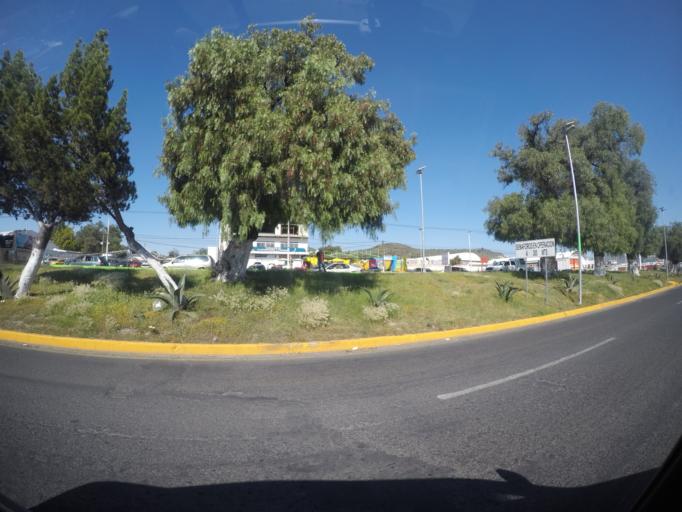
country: MX
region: Hidalgo
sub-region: Mineral de la Reforma
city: Carboneras
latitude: 20.0944
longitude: -98.7145
